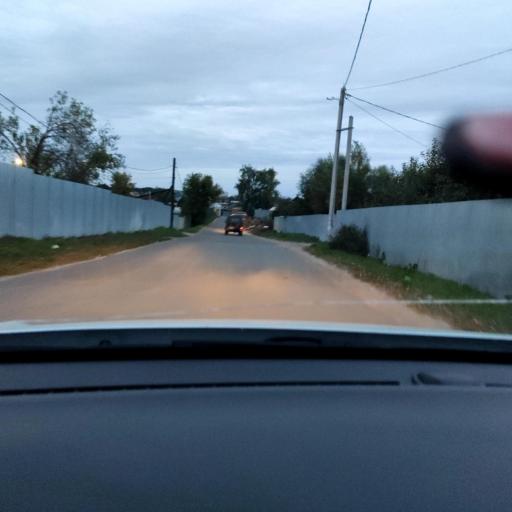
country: RU
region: Mariy-El
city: Volzhsk
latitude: 55.8697
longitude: 48.3661
